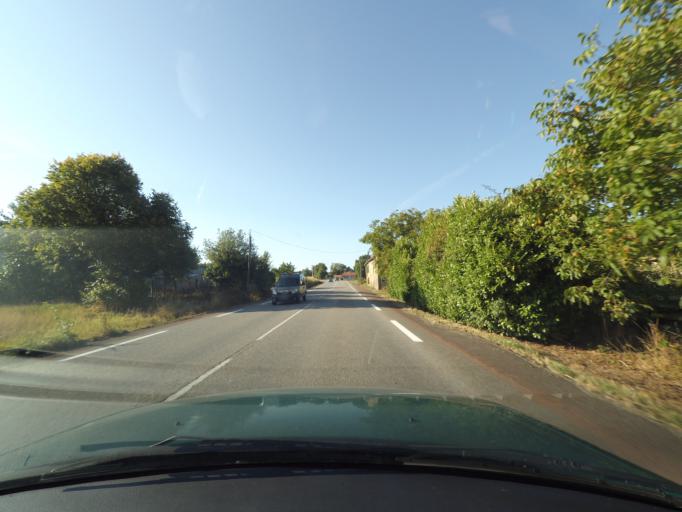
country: FR
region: Poitou-Charentes
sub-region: Departement des Deux-Sevres
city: Viennay
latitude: 46.7247
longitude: -0.2983
